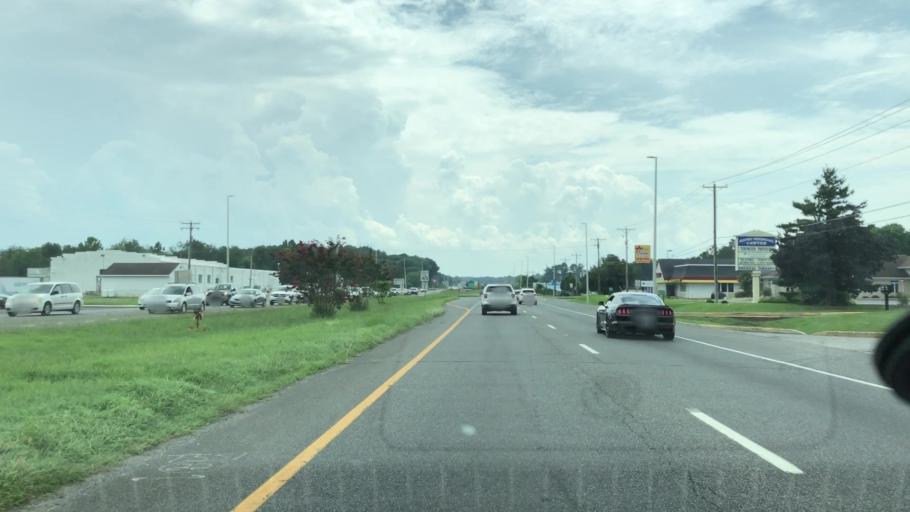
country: US
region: Delaware
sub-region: Sussex County
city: Seaford
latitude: 38.6471
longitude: -75.5940
